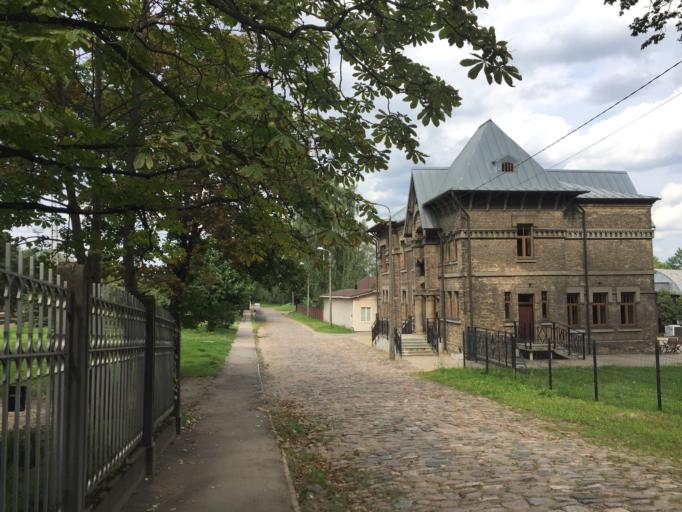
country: LV
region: Riga
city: Riga
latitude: 56.9309
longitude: 24.0881
